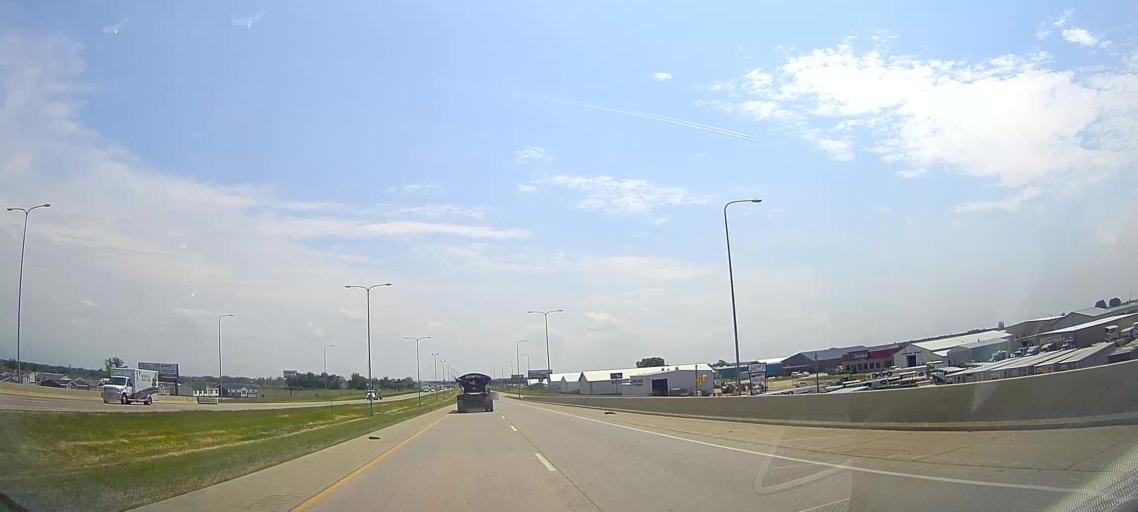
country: US
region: South Dakota
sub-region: Lincoln County
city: Tea
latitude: 43.4588
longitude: -96.7979
